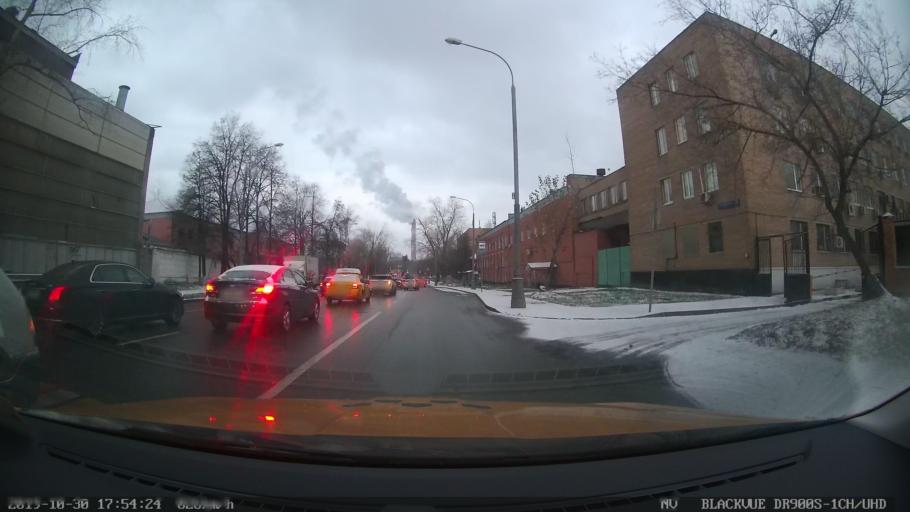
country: RU
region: Moscow
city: Tekstil'shchiki
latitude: 55.7180
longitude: 37.7183
